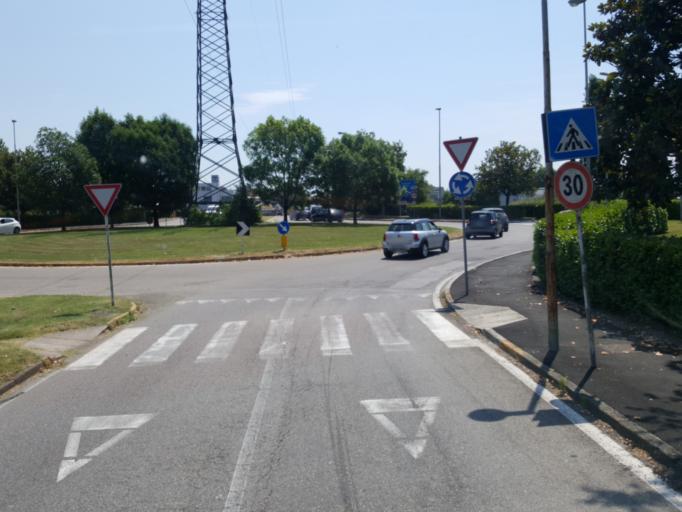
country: IT
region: Lombardy
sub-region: Citta metropolitana di Milano
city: Rozzano
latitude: 45.3960
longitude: 9.1501
